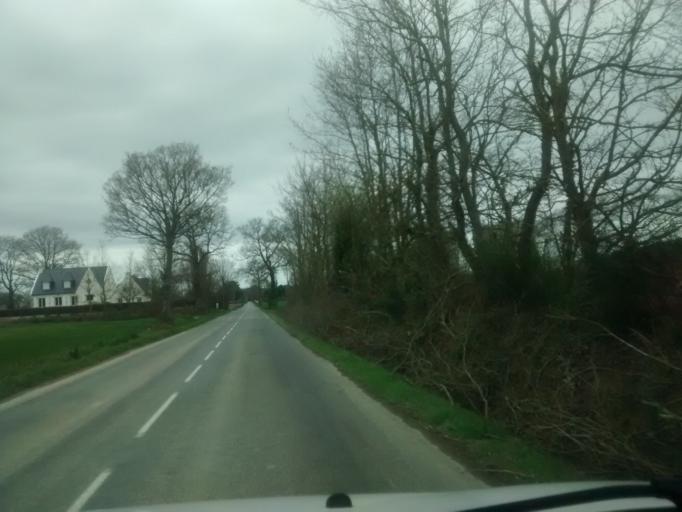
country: FR
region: Brittany
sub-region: Departement d'Ille-et-Vilaine
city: Fouillard
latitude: 48.1705
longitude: -1.5979
